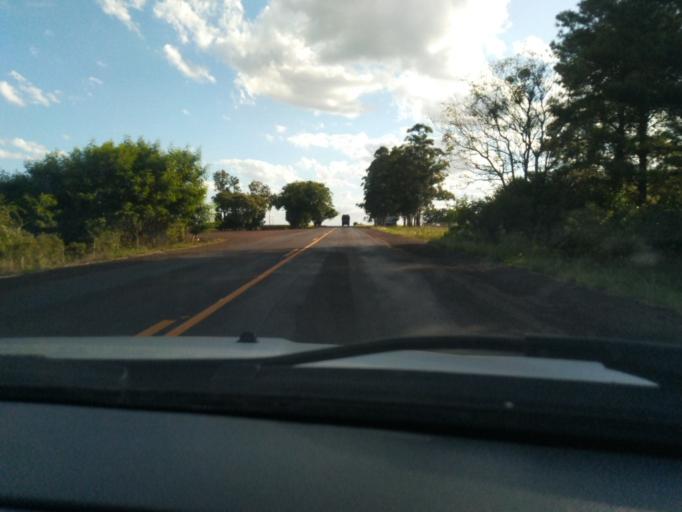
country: AR
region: Corrientes
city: Garruchos
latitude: -28.5509
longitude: -55.5668
